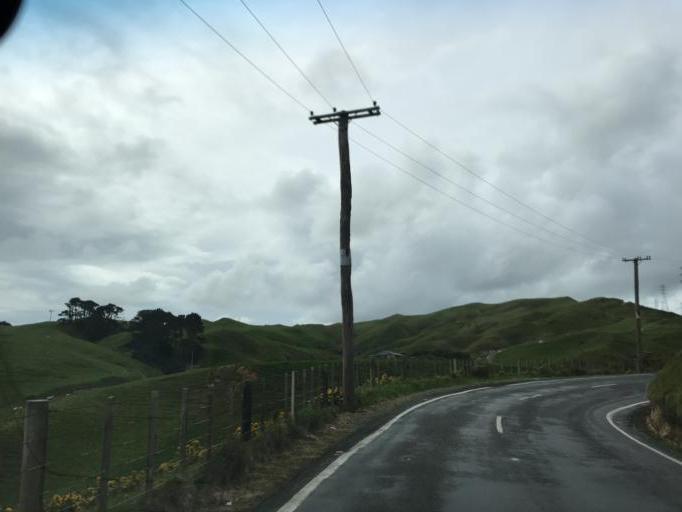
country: NZ
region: Wellington
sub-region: Wellington City
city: Kelburn
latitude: -41.2131
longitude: 174.7897
